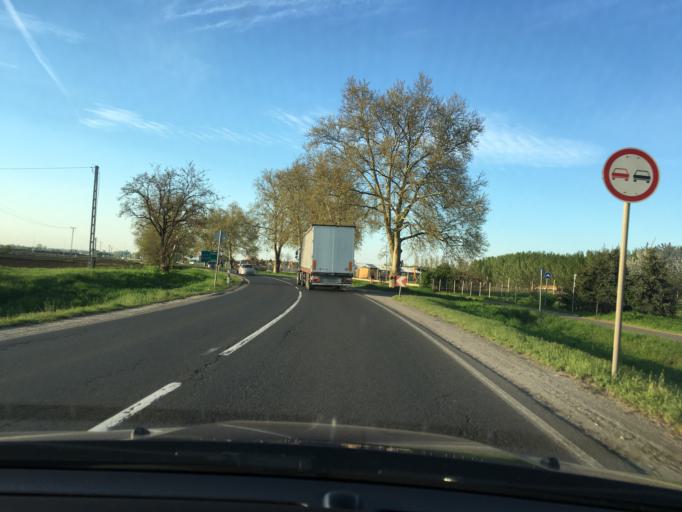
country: HU
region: Hajdu-Bihar
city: Mikepercs
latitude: 47.4582
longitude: 21.6365
